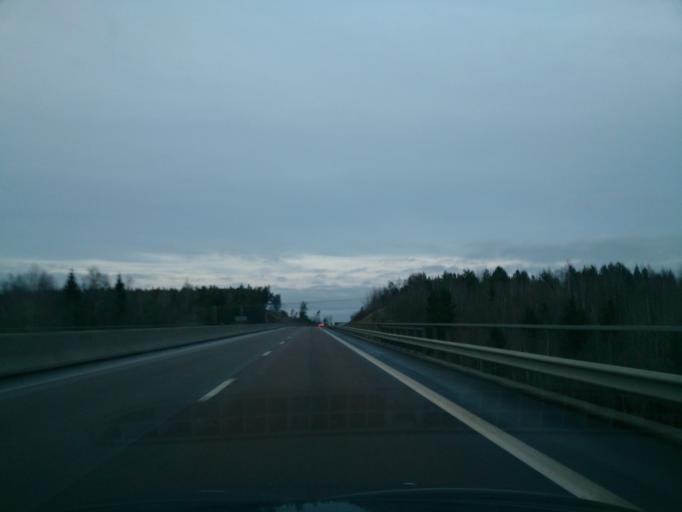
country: SE
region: OEstergoetland
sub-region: Norrkopings Kommun
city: Kimstad
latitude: 58.5111
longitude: 15.9929
